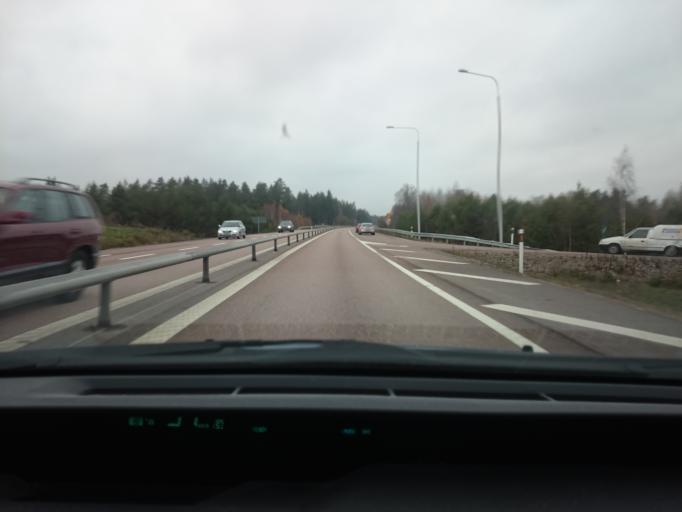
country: SE
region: Dalarna
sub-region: Avesta Kommun
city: Avesta
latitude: 60.1450
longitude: 16.2313
